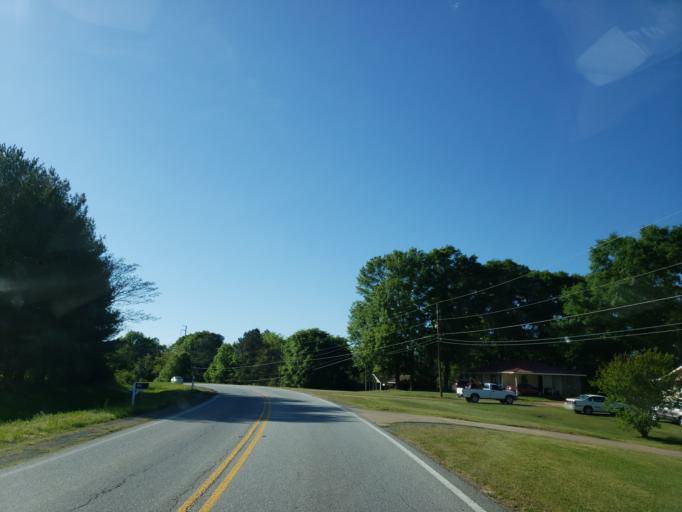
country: US
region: Georgia
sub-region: Polk County
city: Cedartown
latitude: 34.0007
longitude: -85.2381
